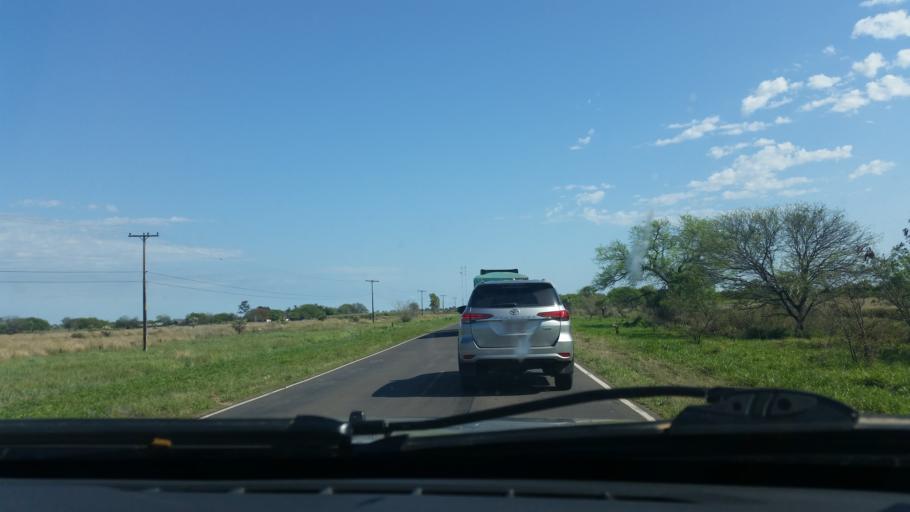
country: PY
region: Presidente Hayes
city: Benjamin Aceval
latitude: -24.6690
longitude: -57.9888
